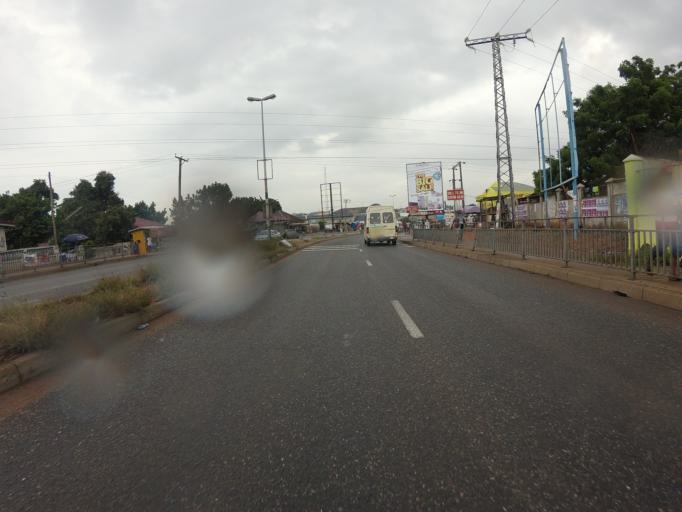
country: GH
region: Greater Accra
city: Dome
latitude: 5.6204
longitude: -0.2256
